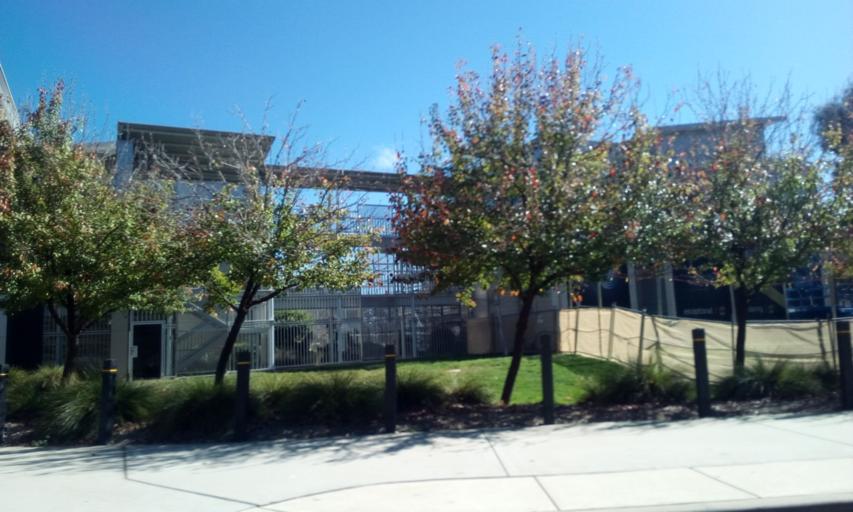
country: AU
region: Australian Capital Territory
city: Kaleen
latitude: -35.2449
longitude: 149.1023
